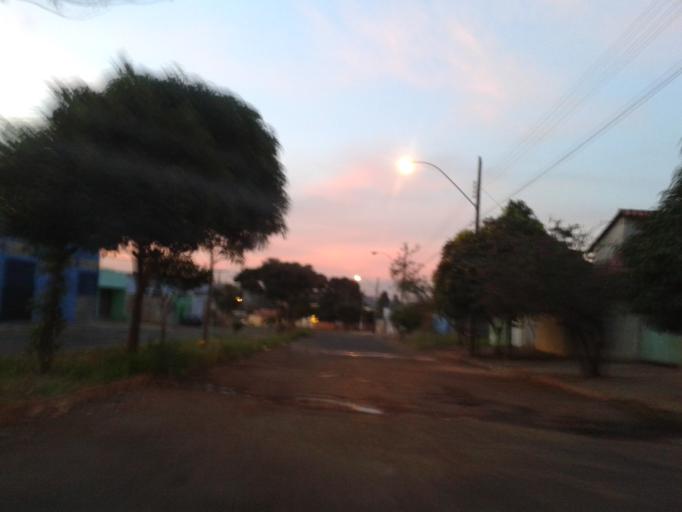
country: BR
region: Goias
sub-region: Goiania
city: Goiania
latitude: -16.6576
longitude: -49.3538
